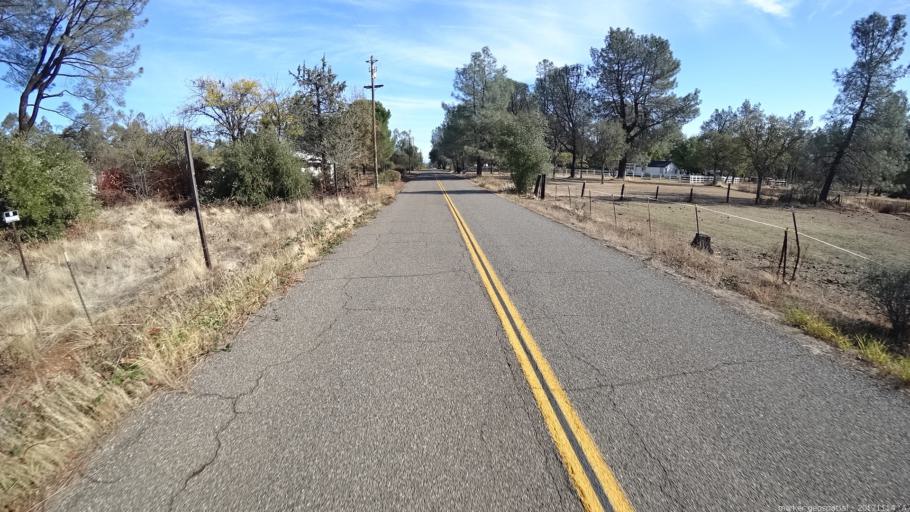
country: US
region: California
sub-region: Shasta County
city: Anderson
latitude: 40.4320
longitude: -122.4221
